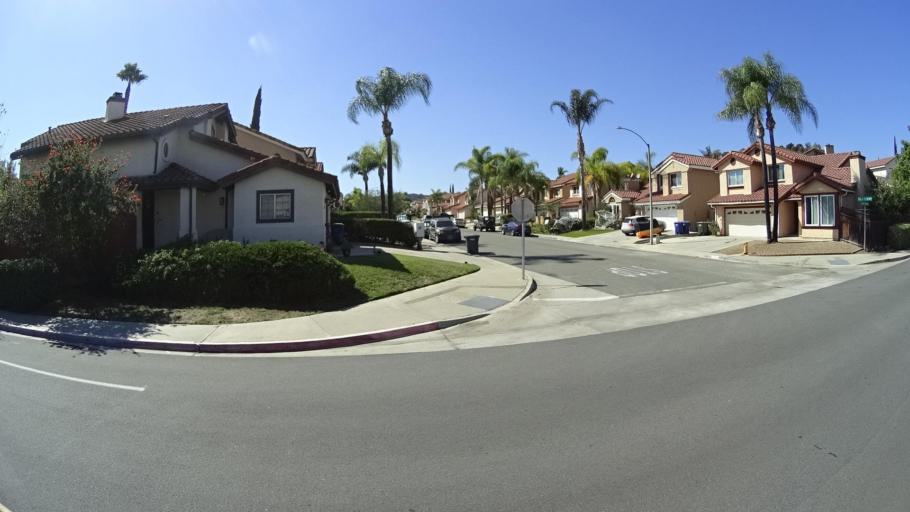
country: US
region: California
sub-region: San Diego County
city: Rancho San Diego
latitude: 32.7501
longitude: -116.9347
